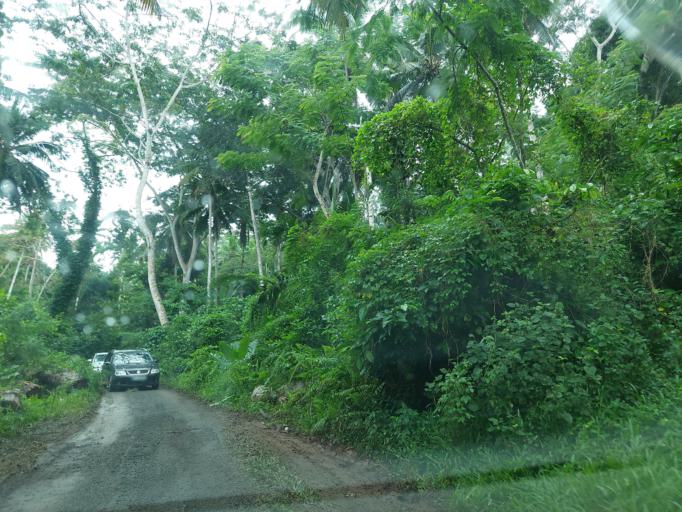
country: YT
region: Tsingoni
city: Tsingoni
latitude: -12.7665
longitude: 45.1222
